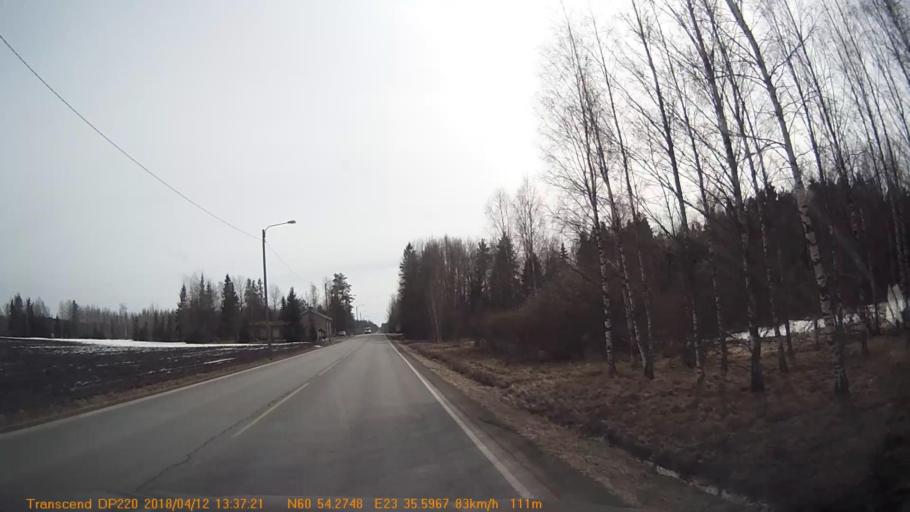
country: FI
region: Haeme
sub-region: Forssa
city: Forssa
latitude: 60.9042
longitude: 23.5934
